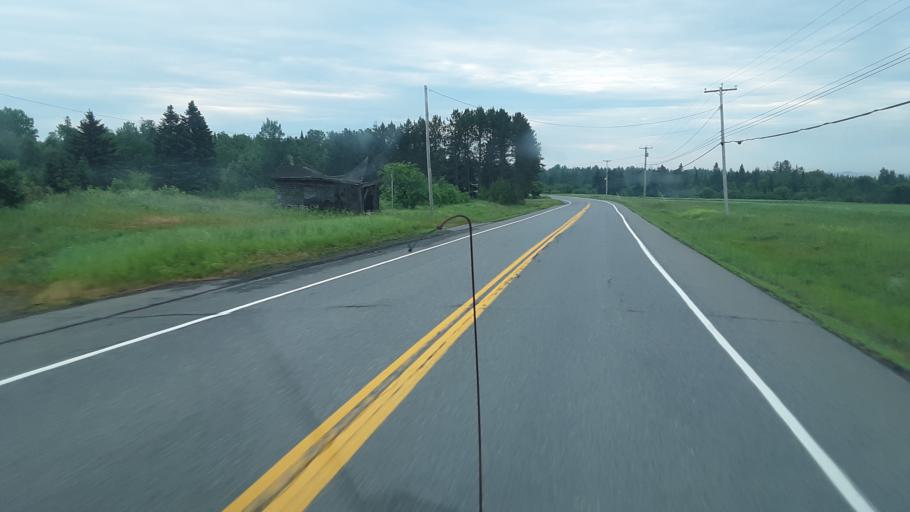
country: US
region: Maine
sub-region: Aroostook County
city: Presque Isle
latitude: 46.5940
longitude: -68.3872
